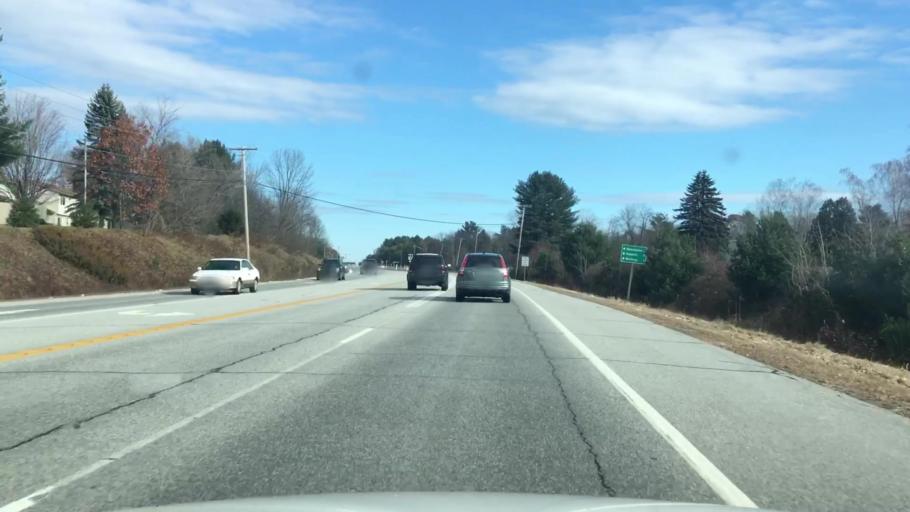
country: US
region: Maine
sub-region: Kennebec County
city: Winthrop
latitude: 44.3044
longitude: -69.9612
